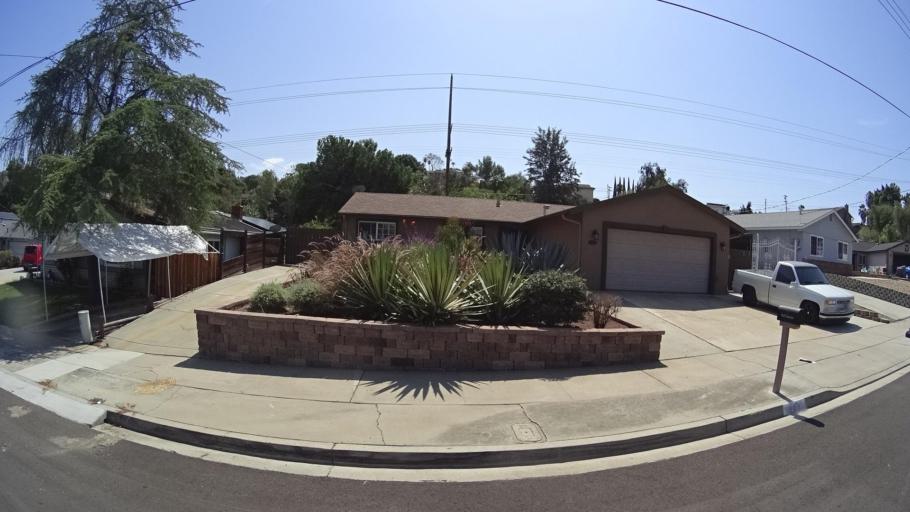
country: US
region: California
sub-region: San Diego County
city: Spring Valley
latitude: 32.7412
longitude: -116.9910
